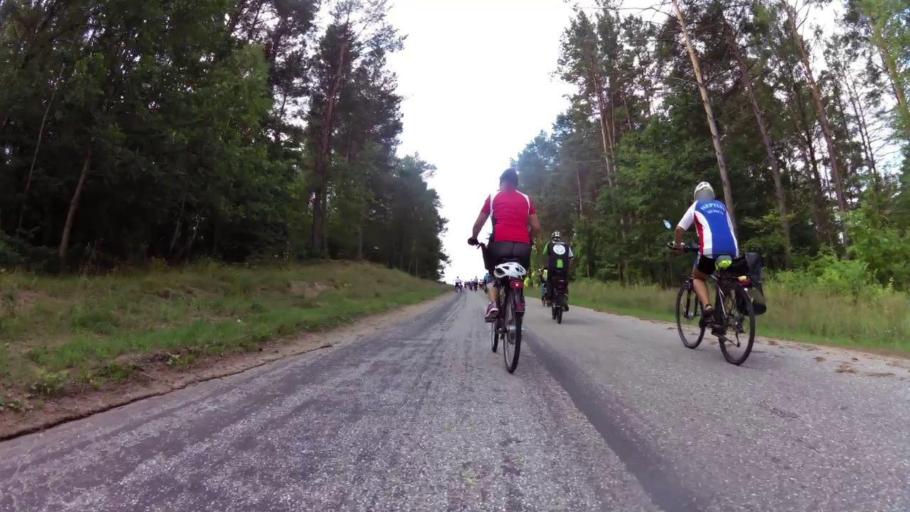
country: PL
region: West Pomeranian Voivodeship
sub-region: Powiat drawski
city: Drawsko Pomorskie
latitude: 53.4581
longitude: 15.7779
